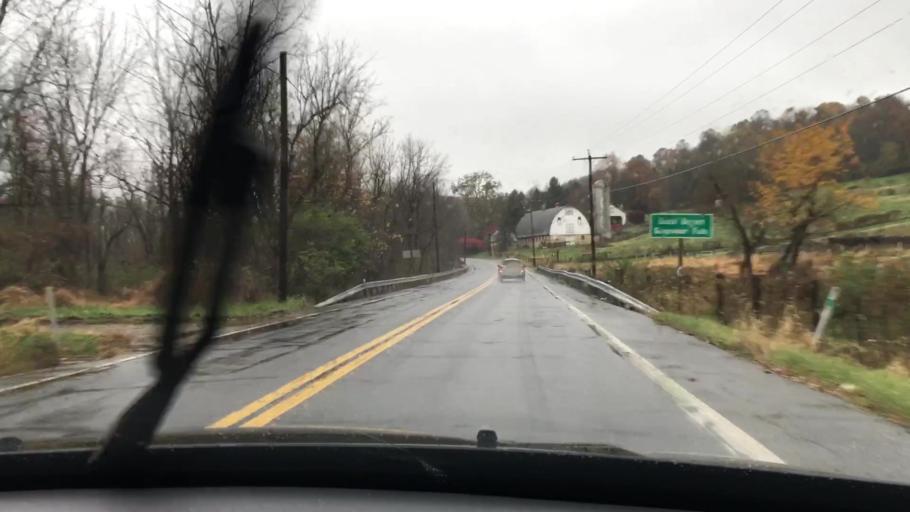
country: US
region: Maryland
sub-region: Carroll County
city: Manchester
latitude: 39.7038
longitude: -76.8632
